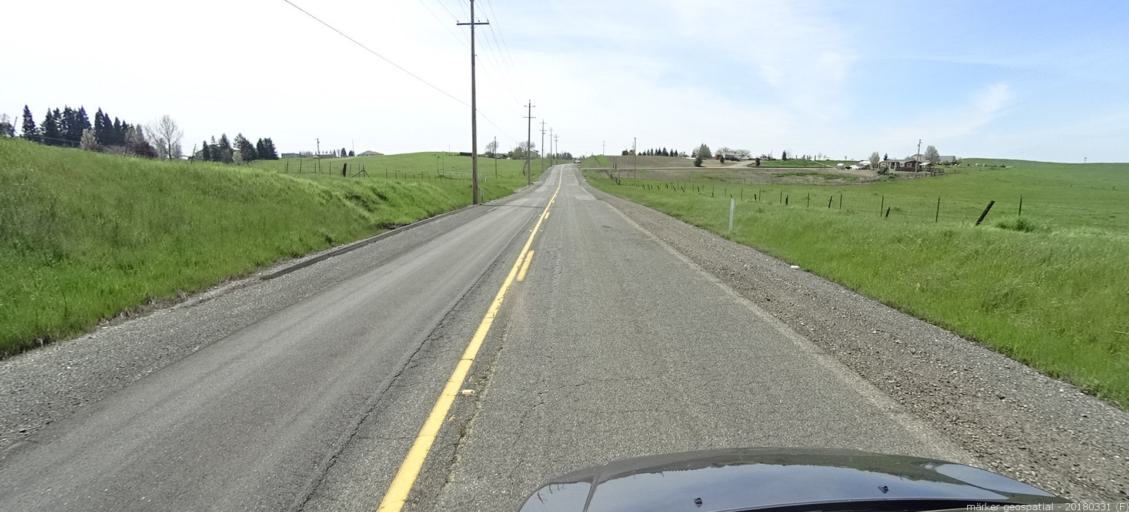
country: US
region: California
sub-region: Sacramento County
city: Rancho Murieta
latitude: 38.5008
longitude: -121.1434
